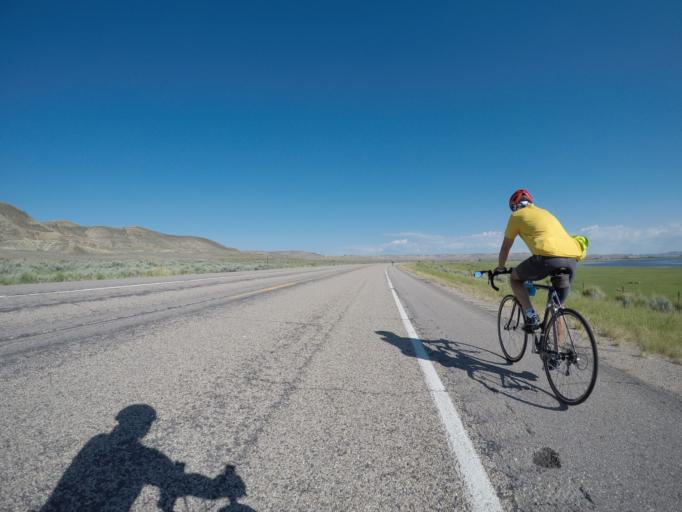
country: US
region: Wyoming
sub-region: Sublette County
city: Marbleton
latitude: 42.1220
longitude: -110.1841
